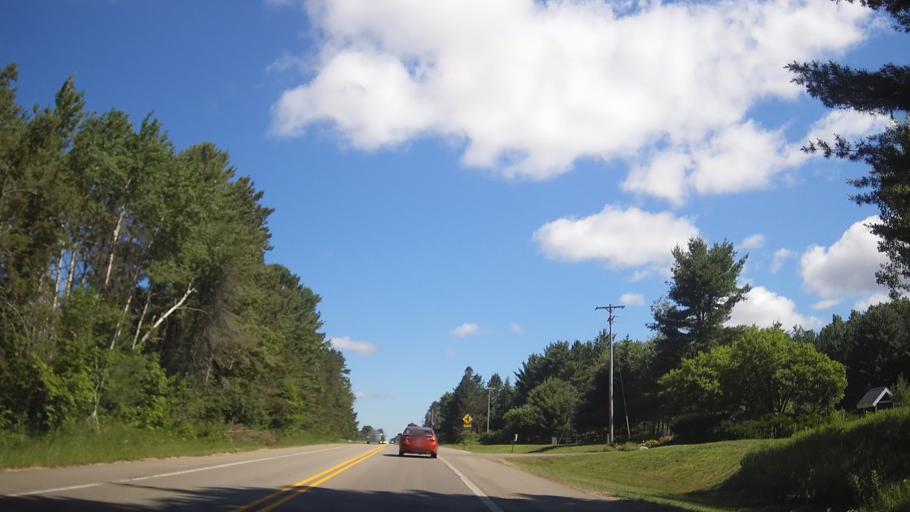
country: US
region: Michigan
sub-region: Cheboygan County
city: Indian River
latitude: 45.4701
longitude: -84.7811
